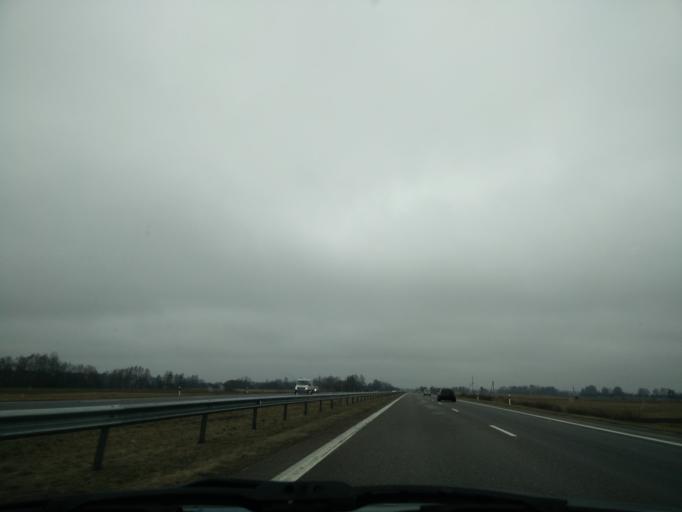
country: LT
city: Skaudvile
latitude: 55.4280
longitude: 22.7560
